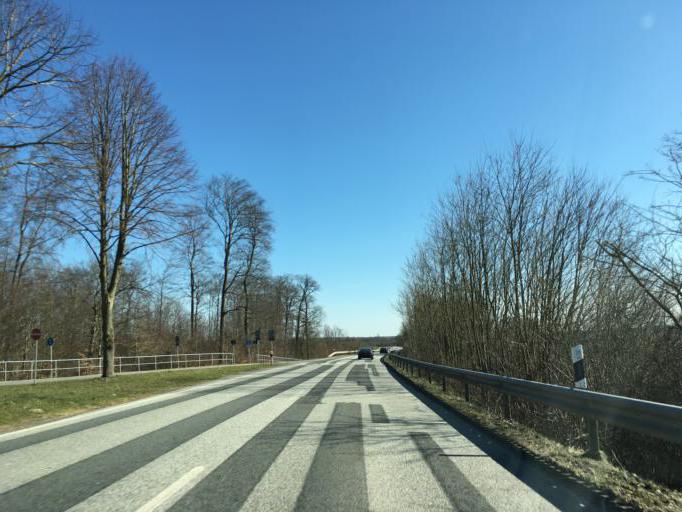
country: DE
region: Schleswig-Holstein
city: Kulpin
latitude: 53.7209
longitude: 10.6789
